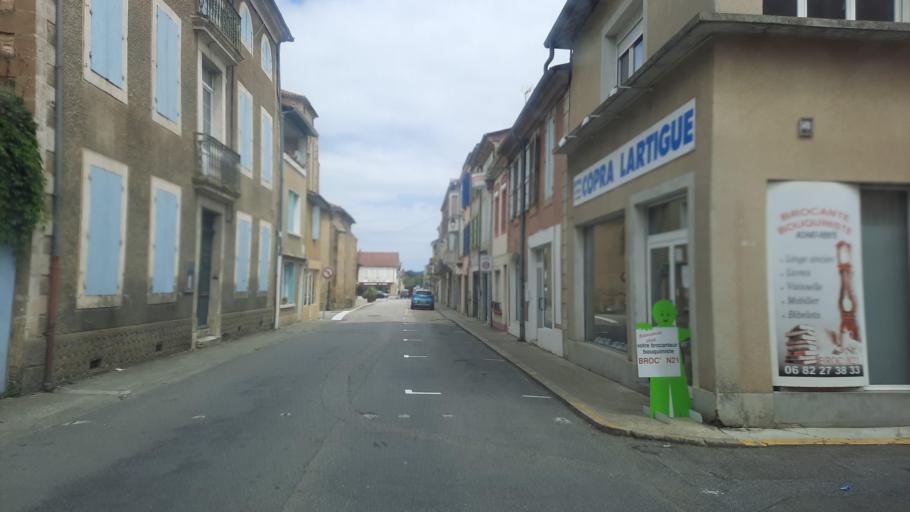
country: FR
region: Midi-Pyrenees
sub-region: Departement des Hautes-Pyrenees
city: Trie-sur-Baise
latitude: 43.3198
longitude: 0.3700
